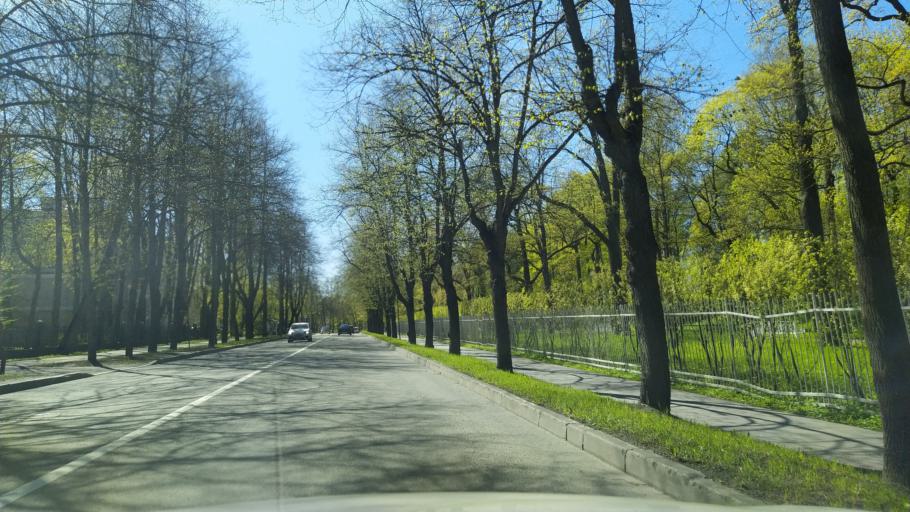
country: RU
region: St.-Petersburg
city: Pushkin
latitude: 59.7111
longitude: 30.4048
